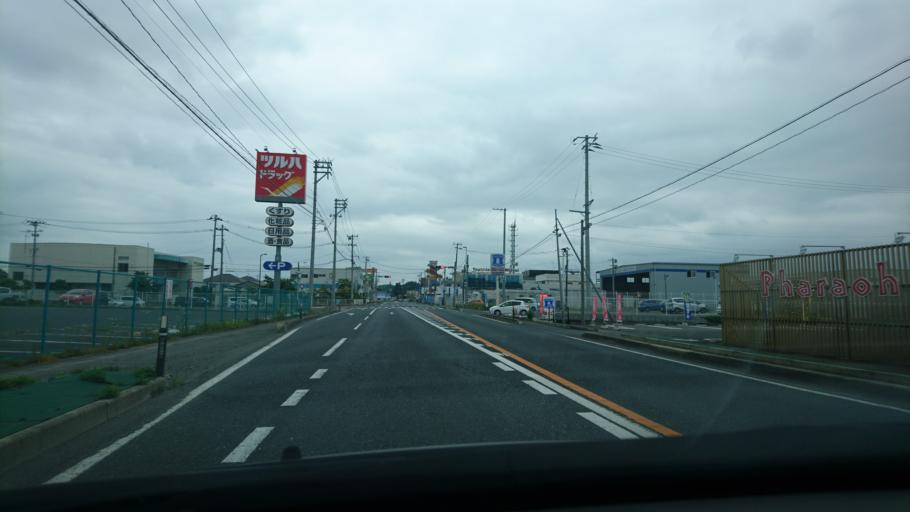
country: JP
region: Miyagi
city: Furukawa
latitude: 38.7472
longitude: 141.0145
